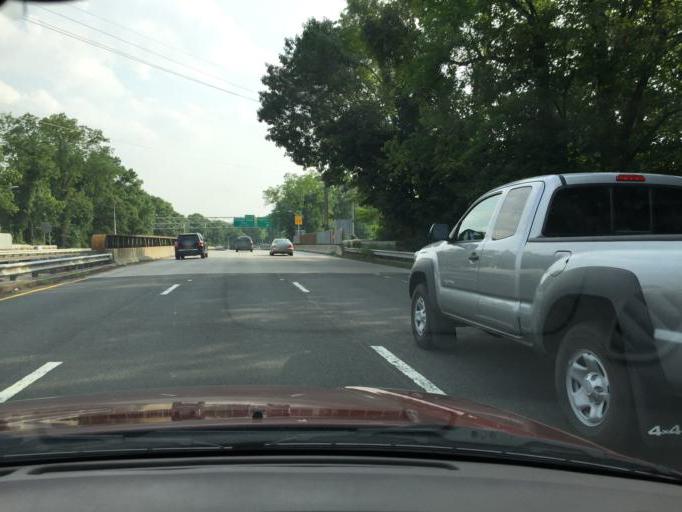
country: US
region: New York
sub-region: Bronx
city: Eastchester
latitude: 40.8584
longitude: -73.8304
